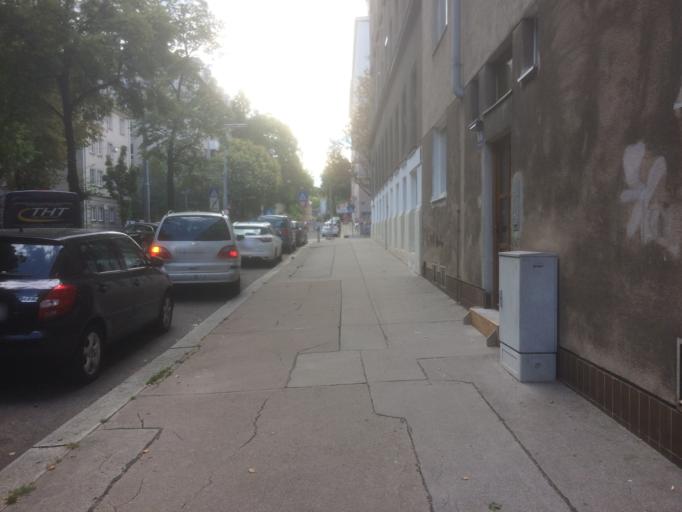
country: AT
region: Vienna
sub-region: Wien Stadt
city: Vienna
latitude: 48.1814
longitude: 16.3458
